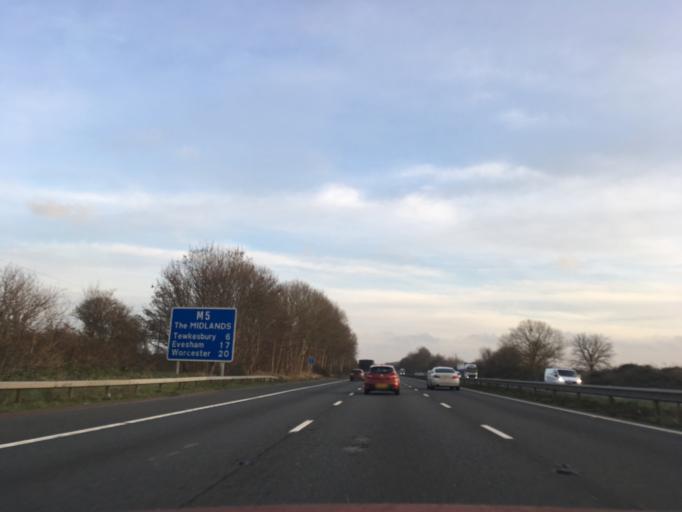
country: GB
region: England
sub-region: Gloucestershire
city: Uckington
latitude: 51.9345
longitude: -2.1338
